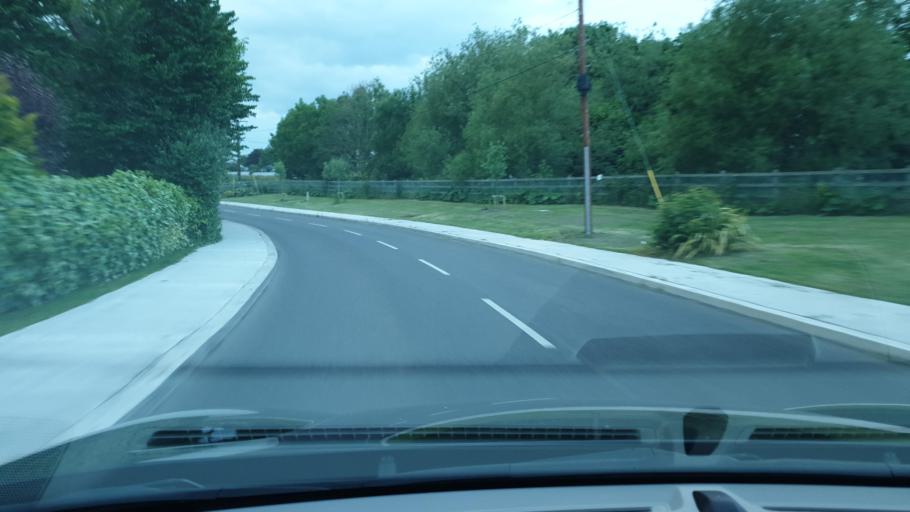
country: IE
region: Leinster
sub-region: An Mhi
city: Ashbourne
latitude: 53.5043
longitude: -6.3826
